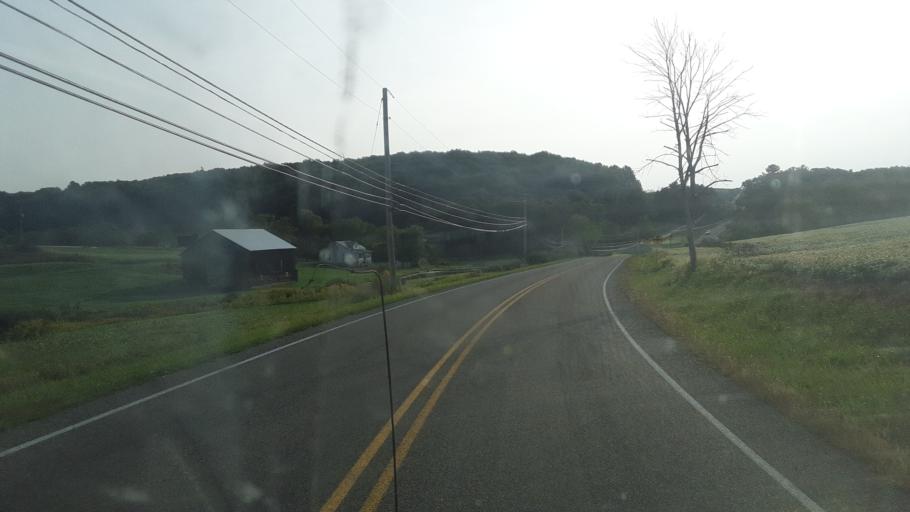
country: US
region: Pennsylvania
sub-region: Jefferson County
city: Punxsutawney
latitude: 40.9610
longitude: -79.0503
